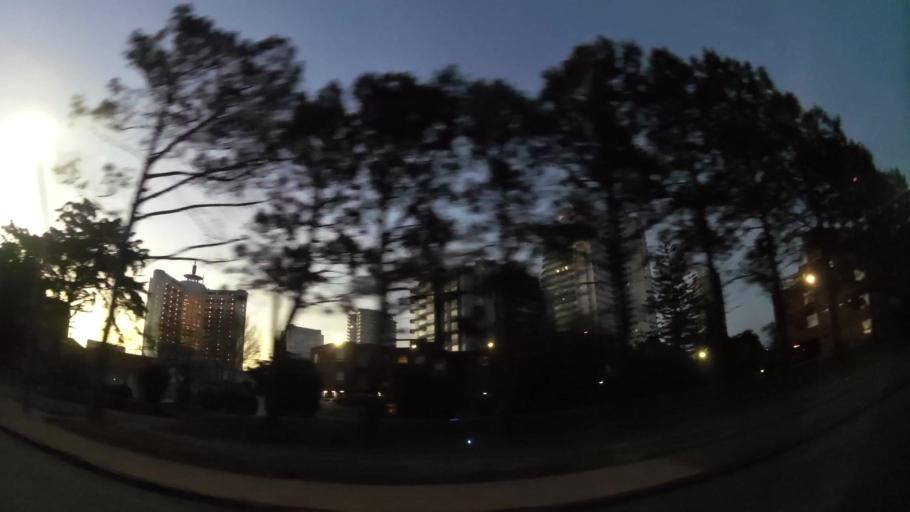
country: UY
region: Maldonado
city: Punta del Este
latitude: -34.9505
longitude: -54.9352
